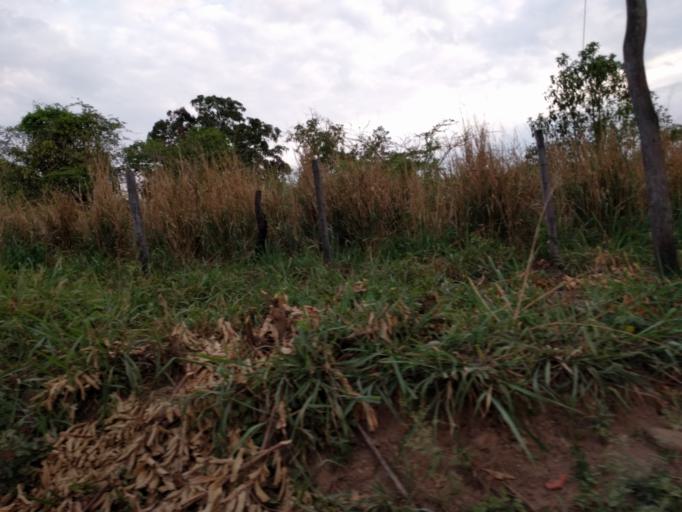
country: BO
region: Santa Cruz
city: Santa Rita
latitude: -17.9466
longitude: -63.3560
